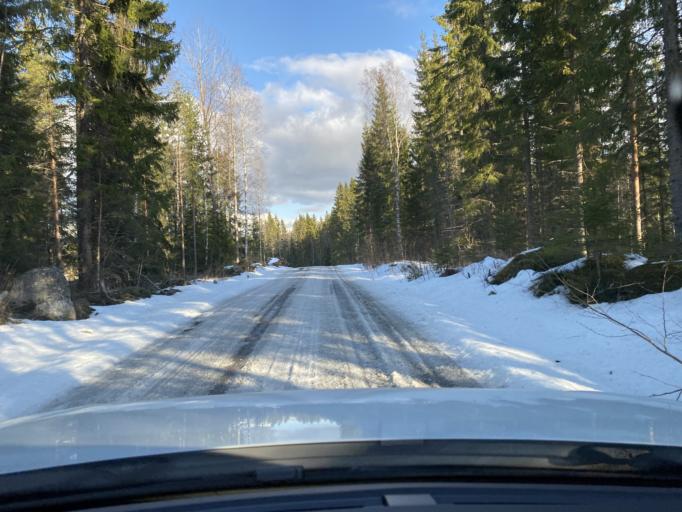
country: FI
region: Pirkanmaa
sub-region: Lounais-Pirkanmaa
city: Mouhijaervi
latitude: 61.4556
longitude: 22.9363
